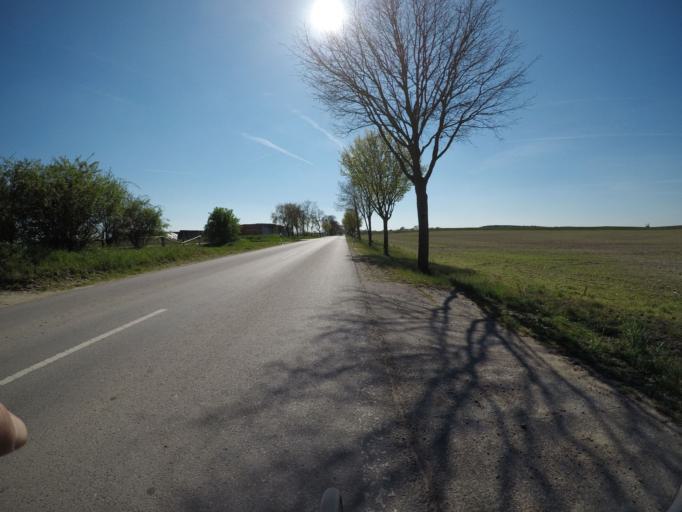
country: DE
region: Brandenburg
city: Strausberg
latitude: 52.5626
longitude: 13.9640
